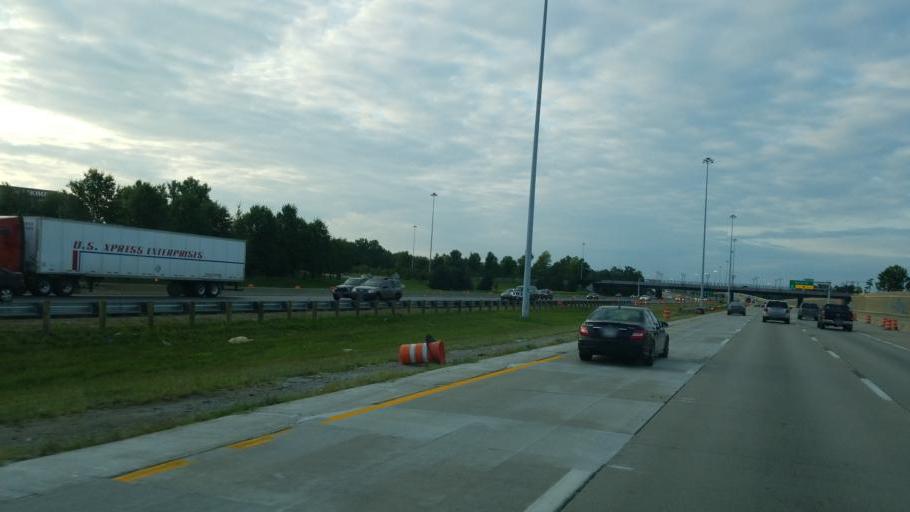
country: US
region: Ohio
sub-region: Franklin County
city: Gahanna
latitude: 40.0449
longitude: -82.9022
